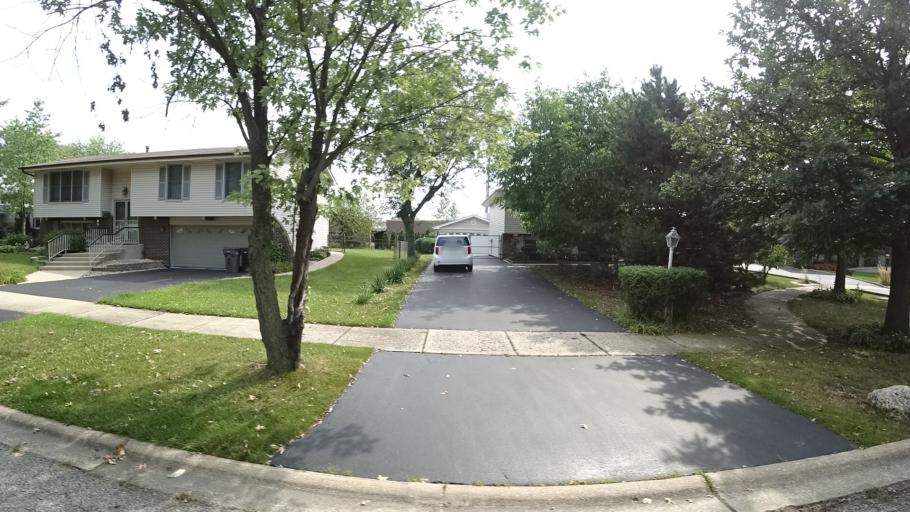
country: US
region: Illinois
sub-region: Cook County
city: Orland Park
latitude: 41.6166
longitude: -87.8587
